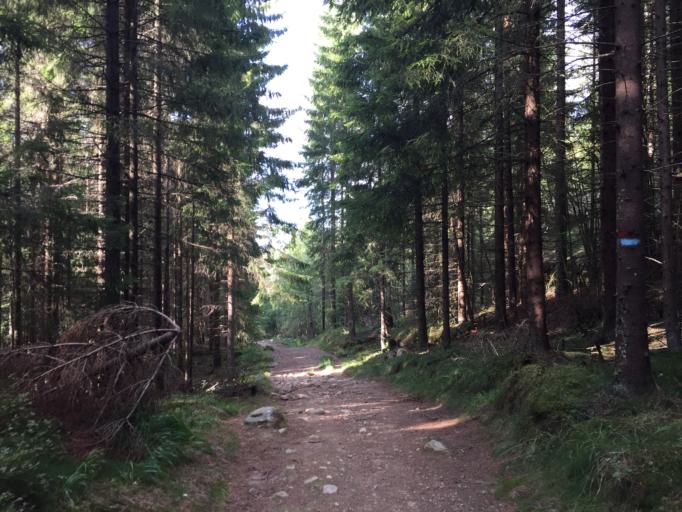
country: NO
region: Akershus
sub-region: Raelingen
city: Fjerdingby
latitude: 59.9171
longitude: 11.0284
